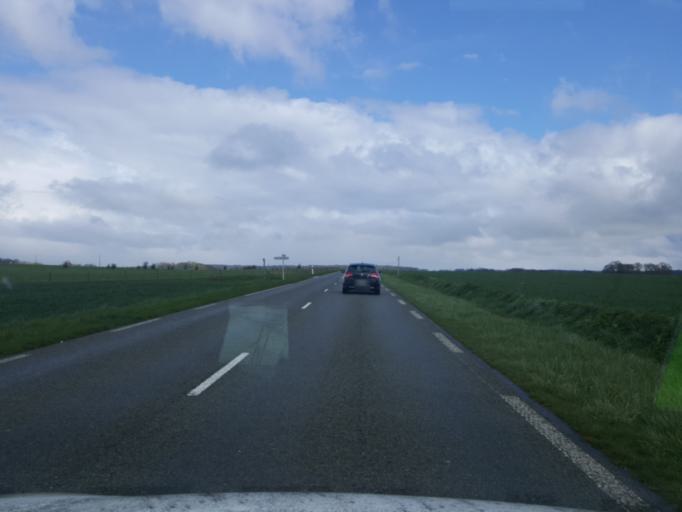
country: FR
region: Picardie
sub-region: Departement de l'Oise
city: Chaumont-en-Vexin
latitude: 49.3256
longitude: 1.8987
